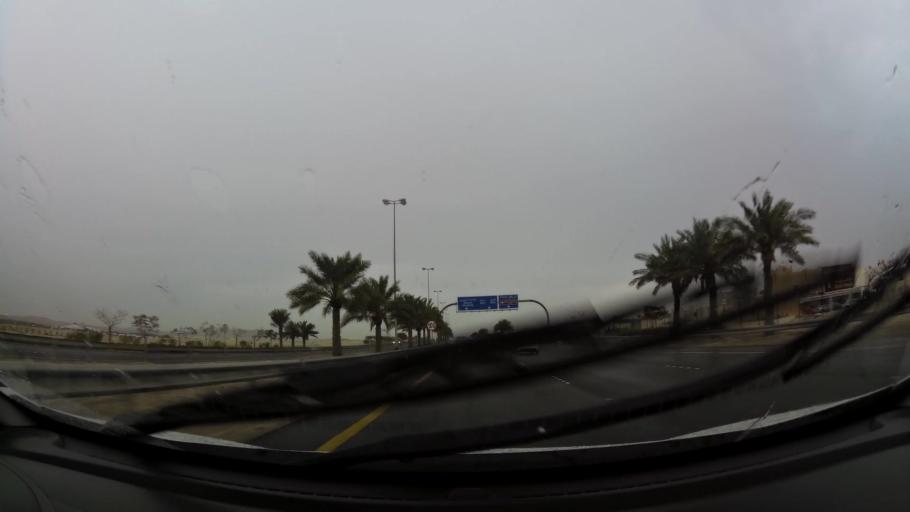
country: BH
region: Central Governorate
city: Dar Kulayb
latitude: 26.0695
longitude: 50.5153
